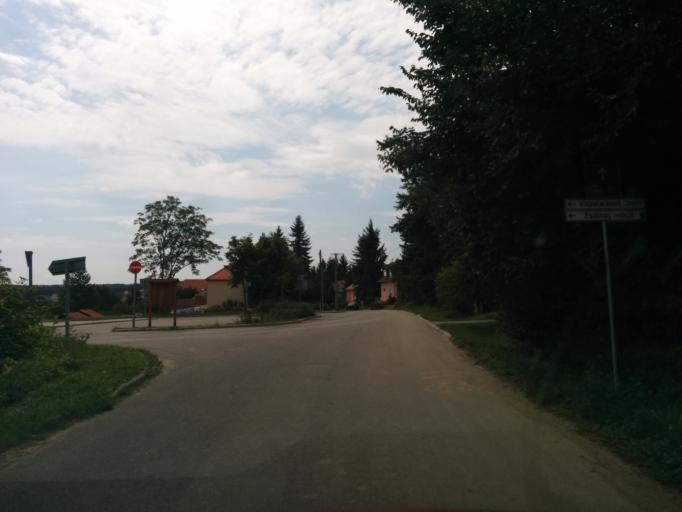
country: HU
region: Gyor-Moson-Sopron
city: Nagycenk
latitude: 47.6586
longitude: 16.6667
